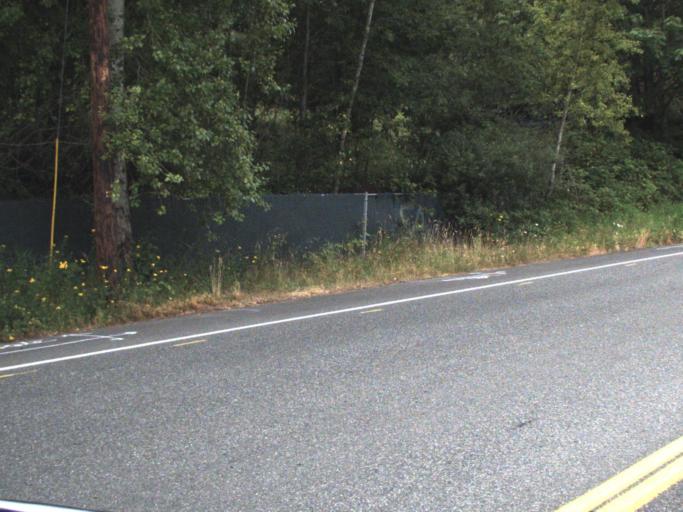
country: US
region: Washington
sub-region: King County
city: Woodinville
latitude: 47.7487
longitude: -122.1665
